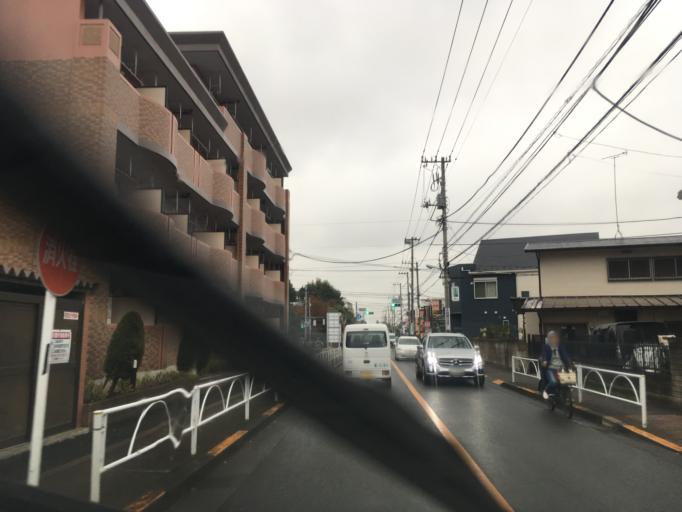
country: JP
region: Tokyo
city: Kokubunji
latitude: 35.7174
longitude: 139.4299
